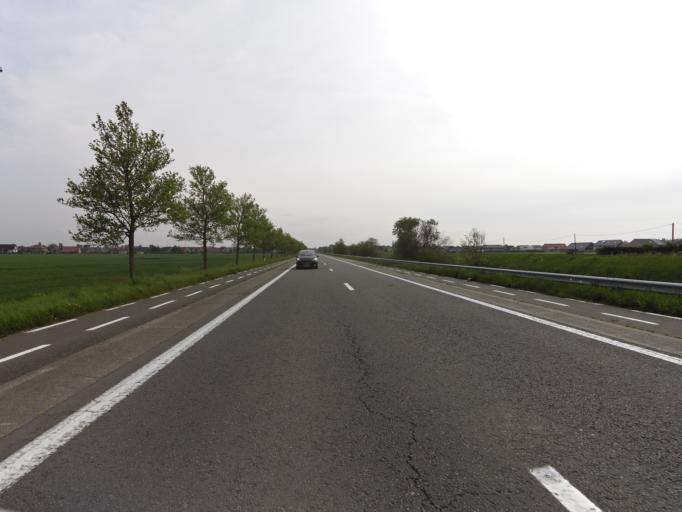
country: BE
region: Flanders
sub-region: Provincie West-Vlaanderen
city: Veurne
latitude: 51.0831
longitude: 2.6720
